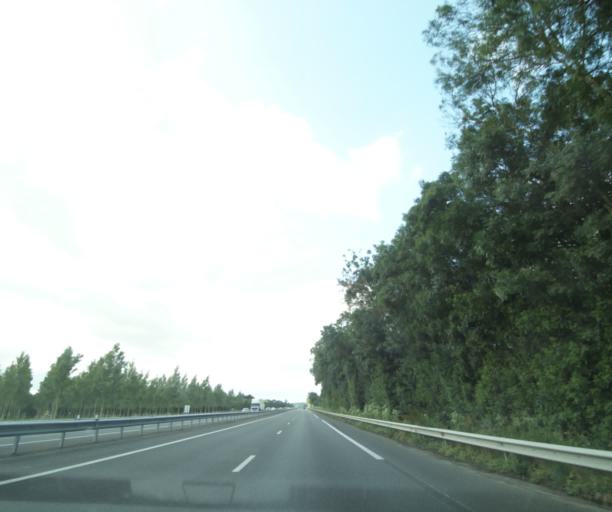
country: FR
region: Pays de la Loire
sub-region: Departement de Maine-et-Loire
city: Vivy
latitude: 47.3007
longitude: -0.0382
